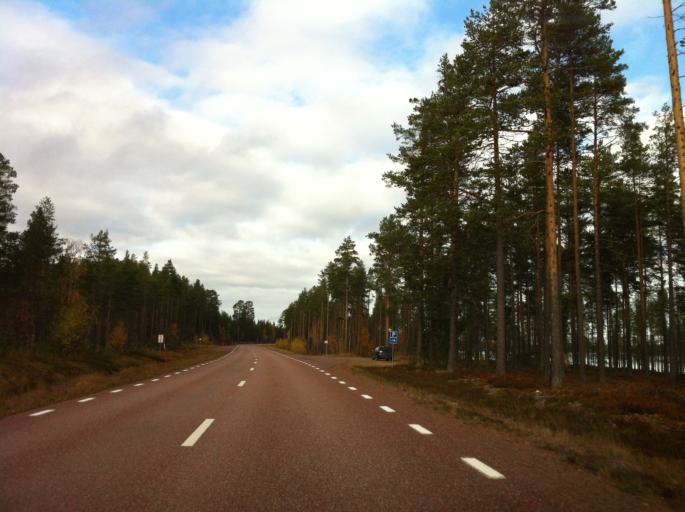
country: SE
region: Dalarna
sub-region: Alvdalens Kommun
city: AElvdalen
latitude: 61.5412
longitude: 13.3421
